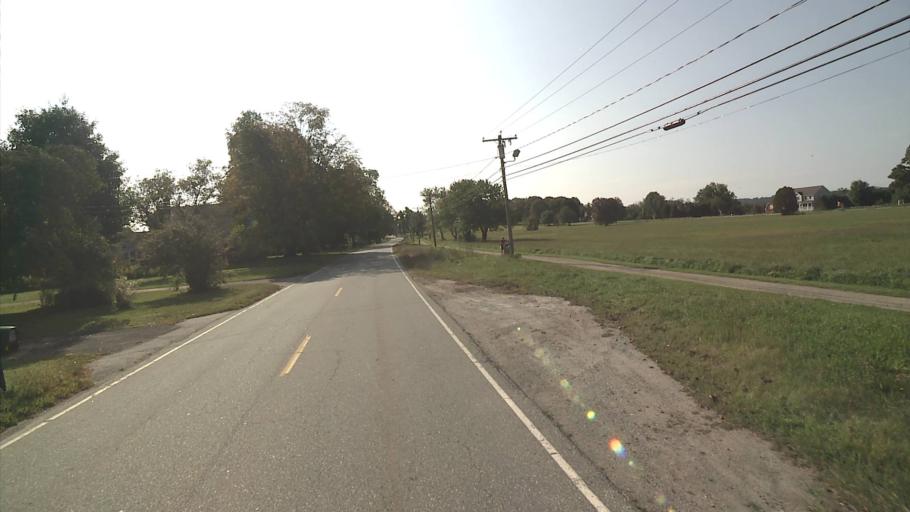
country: US
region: Connecticut
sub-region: Windham County
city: South Windham
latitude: 41.6405
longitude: -72.2163
